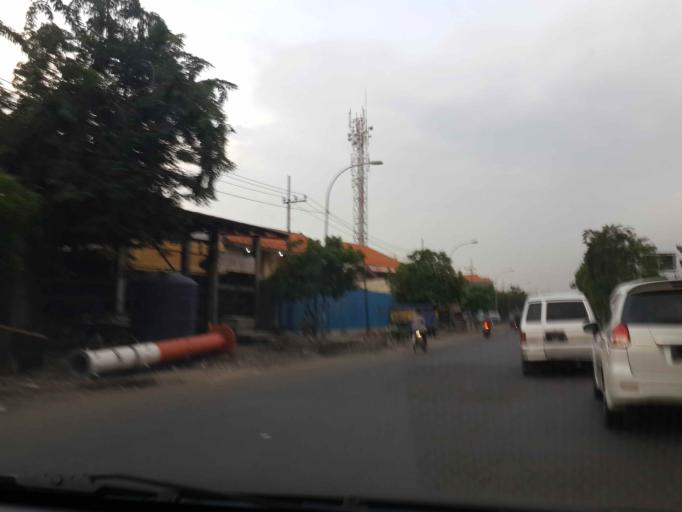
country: ID
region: East Java
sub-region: Kota Surabaya
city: Surabaya
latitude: -7.2450
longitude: 112.7150
